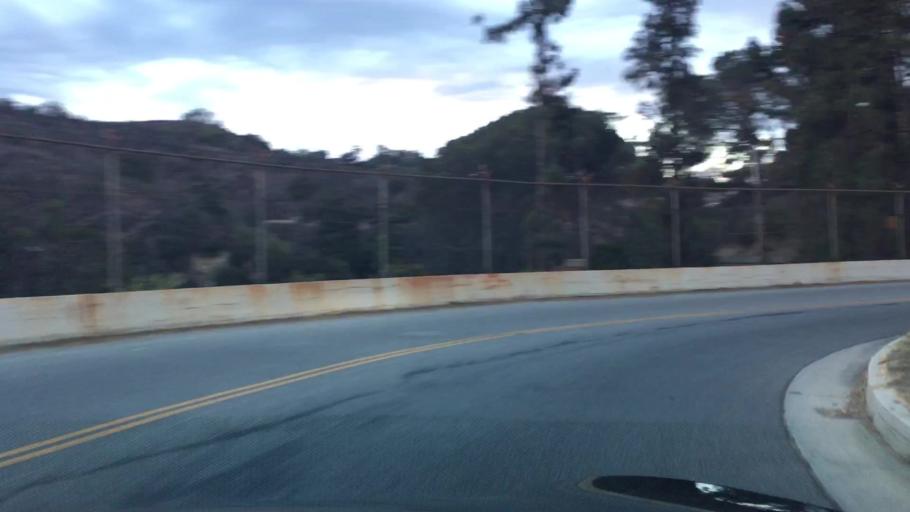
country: US
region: California
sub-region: Los Angeles County
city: Universal City
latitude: 34.1255
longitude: -118.3343
